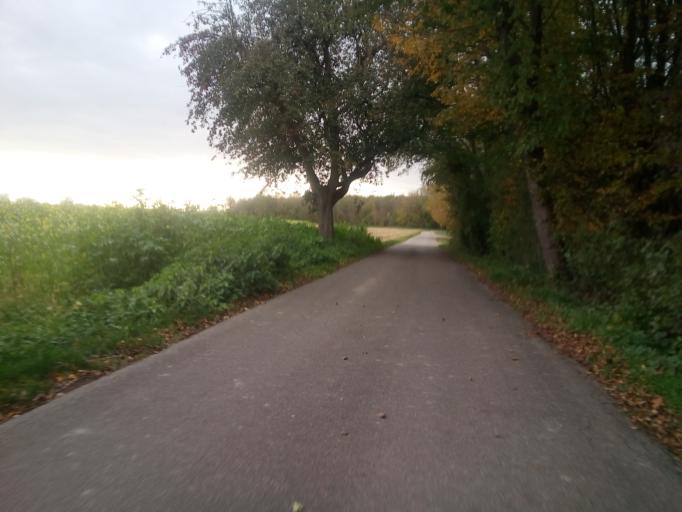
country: DE
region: Baden-Wuerttemberg
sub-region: Karlsruhe Region
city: Schwarzach
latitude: 48.7654
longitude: 8.0283
